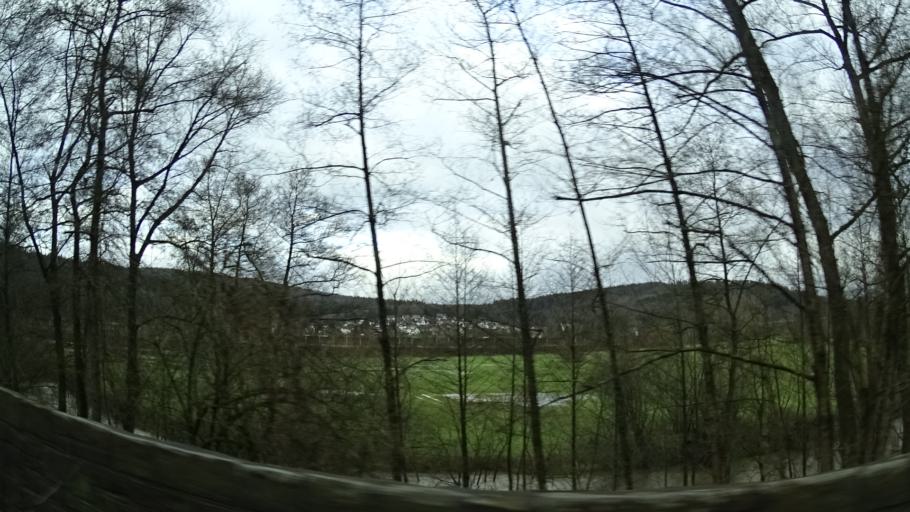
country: DE
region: Hesse
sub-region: Regierungsbezirk Darmstadt
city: Wachtersbach
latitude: 50.2217
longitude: 9.2531
